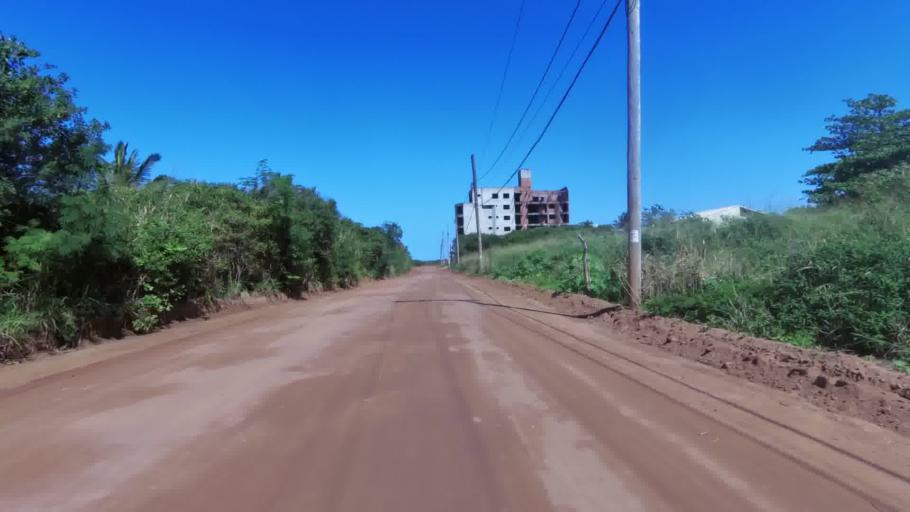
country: BR
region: Espirito Santo
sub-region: Piuma
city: Piuma
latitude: -20.8316
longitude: -40.6205
